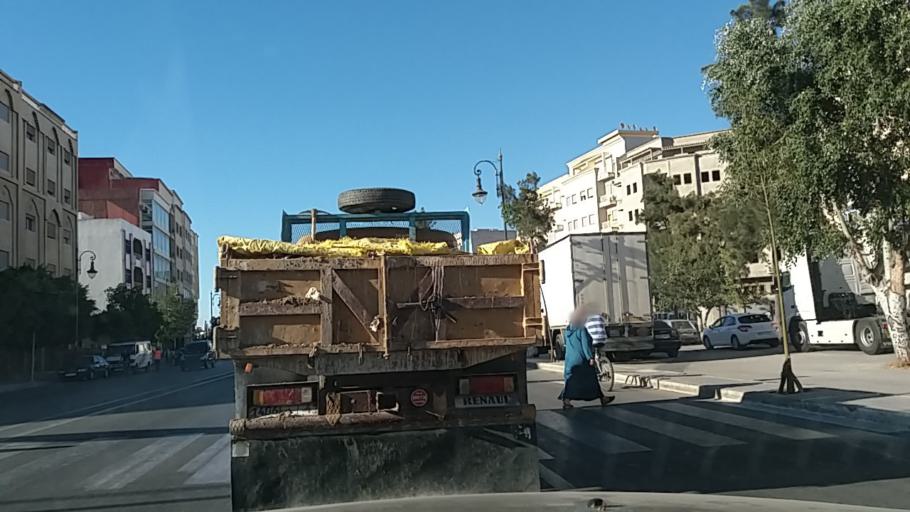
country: MA
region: Tanger-Tetouan
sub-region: Tanger-Assilah
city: Tangier
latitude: 35.7452
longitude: -5.7989
